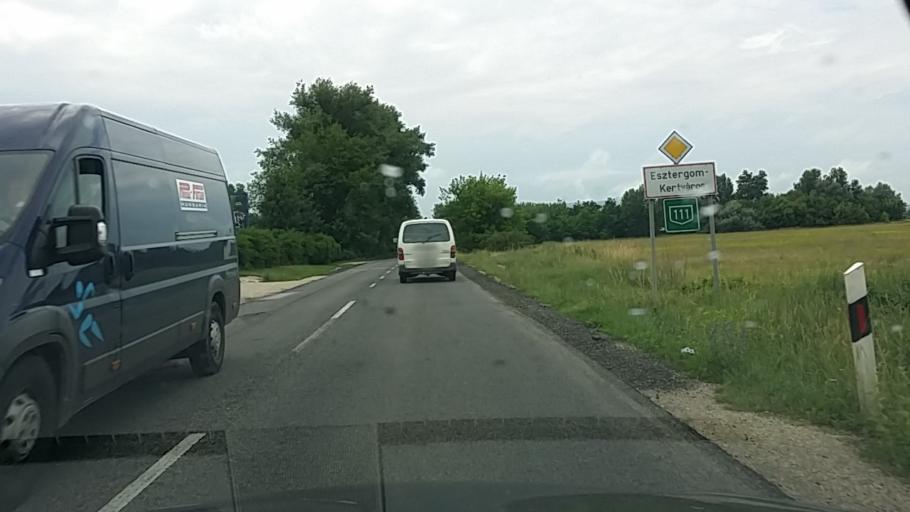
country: HU
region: Komarom-Esztergom
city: Dorog
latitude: 47.7568
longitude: 18.7343
